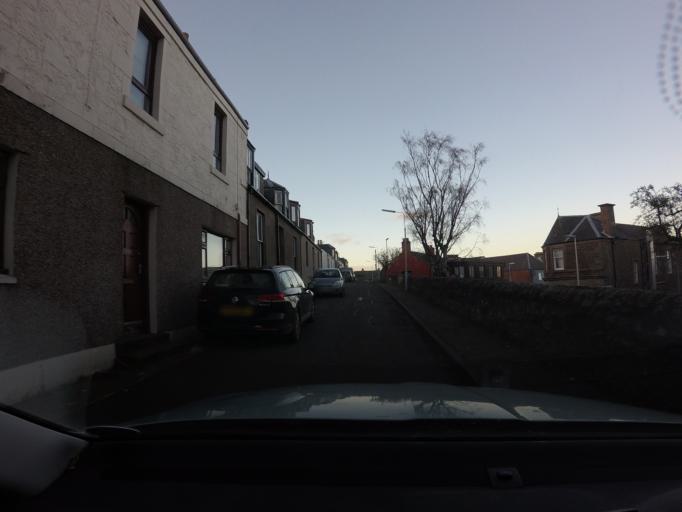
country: GB
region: Scotland
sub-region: Fife
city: Tayport
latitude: 56.4498
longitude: -2.8816
